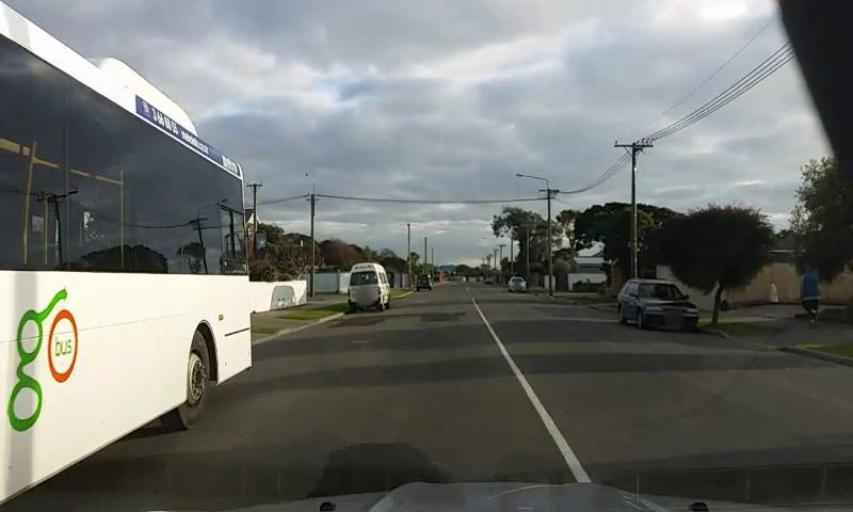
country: NZ
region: Canterbury
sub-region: Christchurch City
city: Christchurch
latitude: -43.5213
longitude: 172.7318
